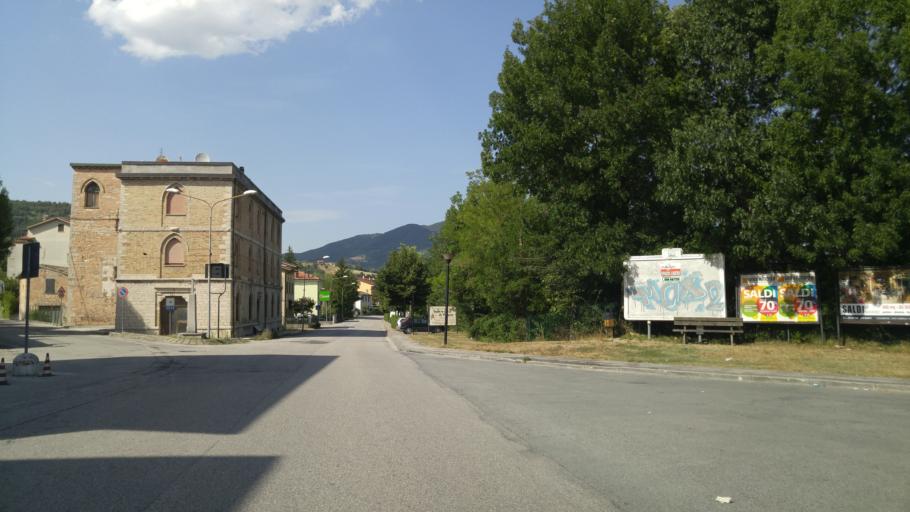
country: IT
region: The Marches
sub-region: Provincia di Pesaro e Urbino
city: Acqualagna
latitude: 43.6193
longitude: 12.6733
